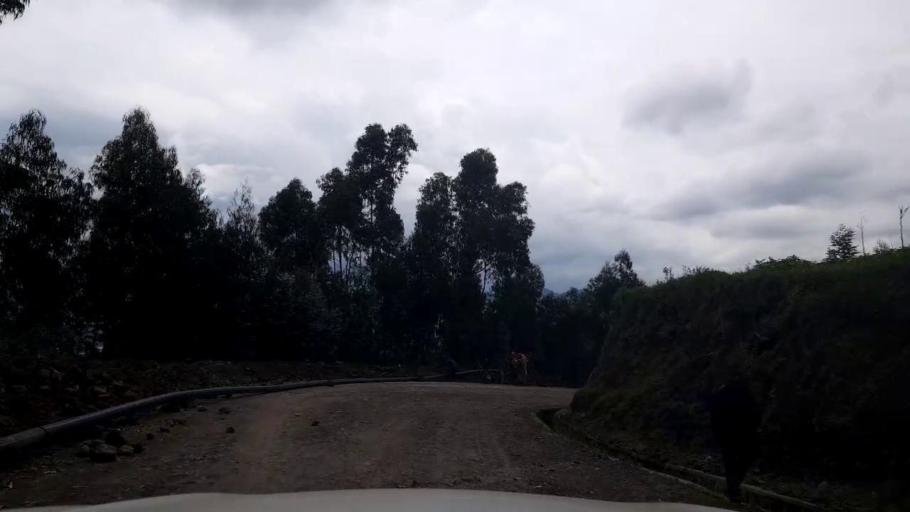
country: RW
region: Northern Province
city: Musanze
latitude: -1.5360
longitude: 29.5332
